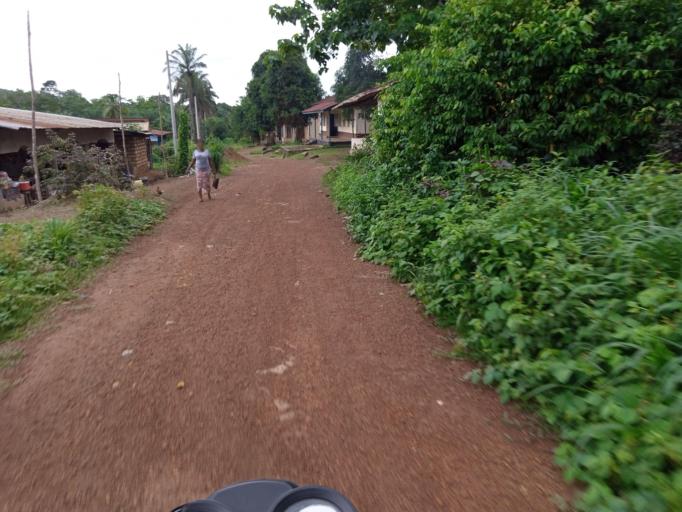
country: SL
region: Southern Province
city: Moyamba
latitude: 8.1662
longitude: -12.4272
